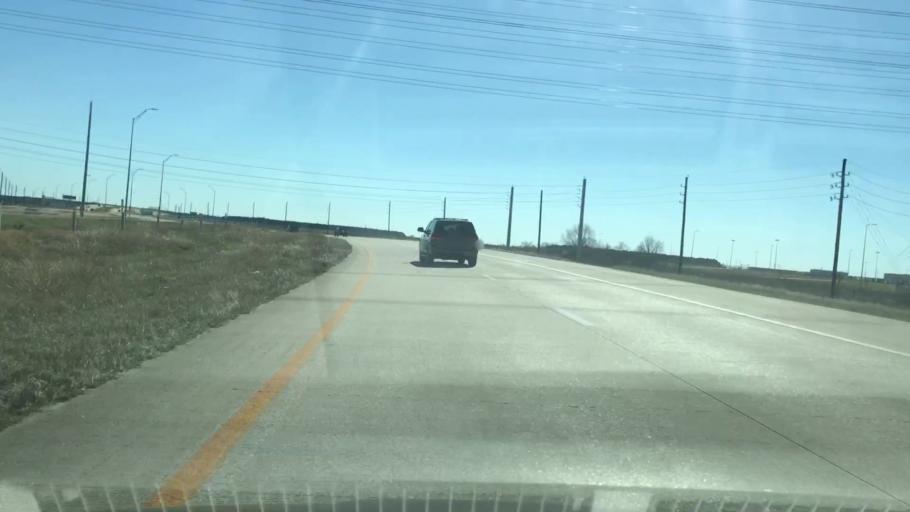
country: US
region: Texas
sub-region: Harris County
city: Cypress
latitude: 29.9134
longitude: -95.7622
